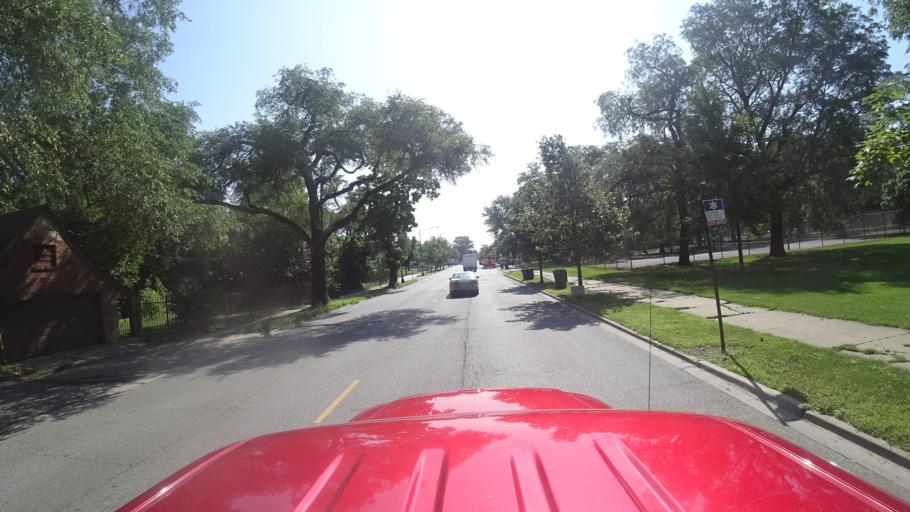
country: US
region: Illinois
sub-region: Cook County
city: Chicago
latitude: 41.7939
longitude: -87.6866
